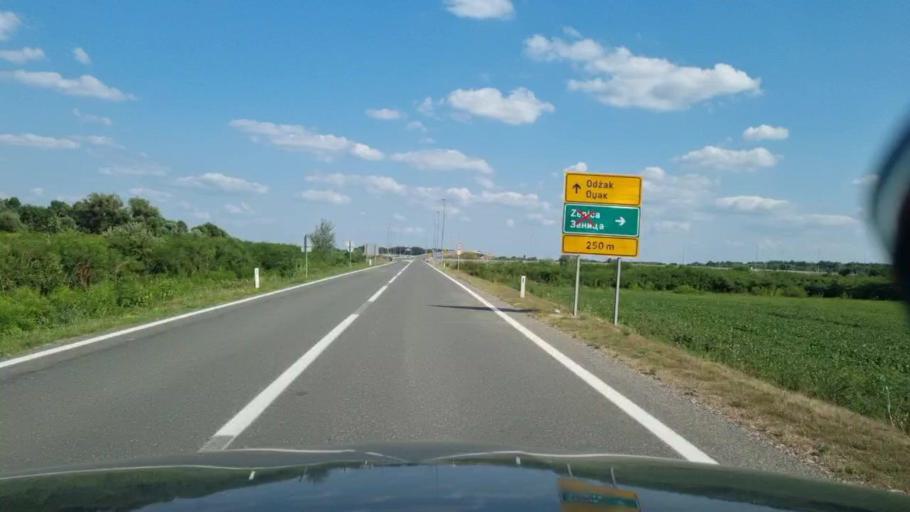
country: BA
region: Federation of Bosnia and Herzegovina
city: Odzak
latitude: 45.1040
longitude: 18.2927
